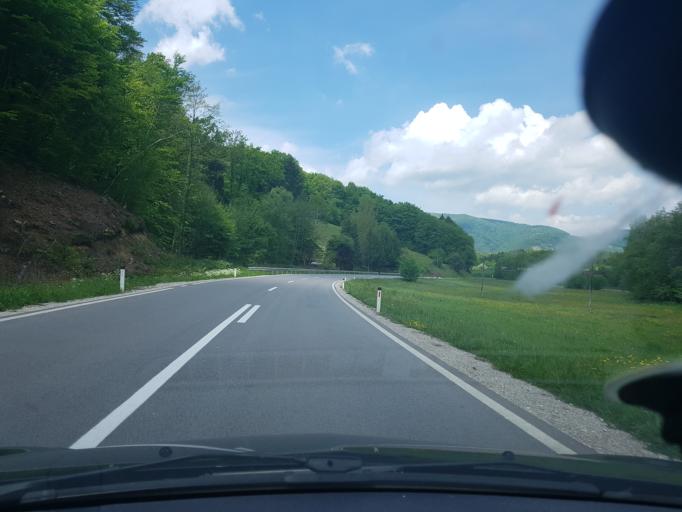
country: SI
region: Rogatec
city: Rogatec
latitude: 46.2312
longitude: 15.6737
